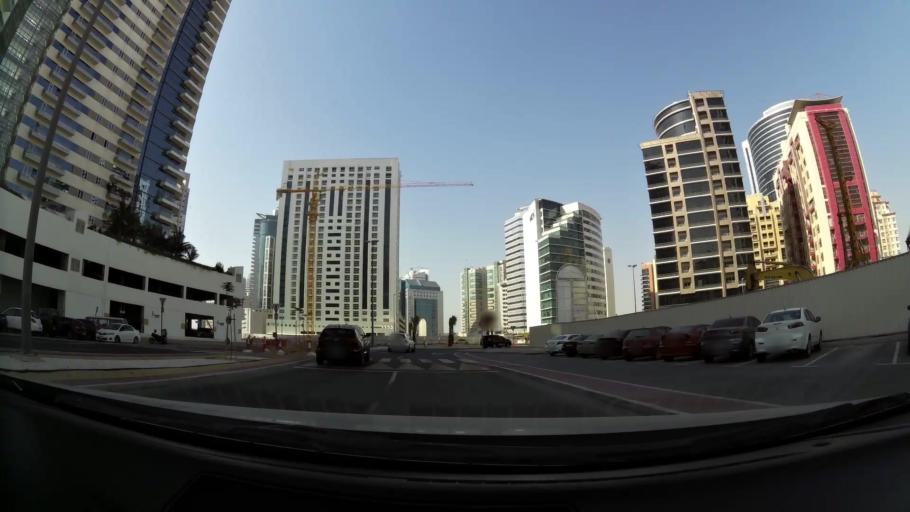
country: AE
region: Dubai
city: Dubai
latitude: 25.0955
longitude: 55.1776
